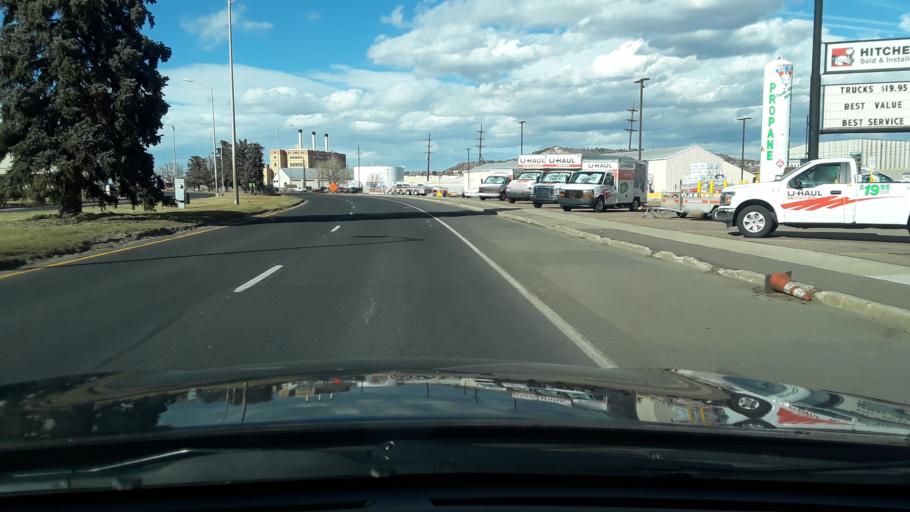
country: US
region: Colorado
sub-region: El Paso County
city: Colorado Springs
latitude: 38.8764
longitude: -104.8189
